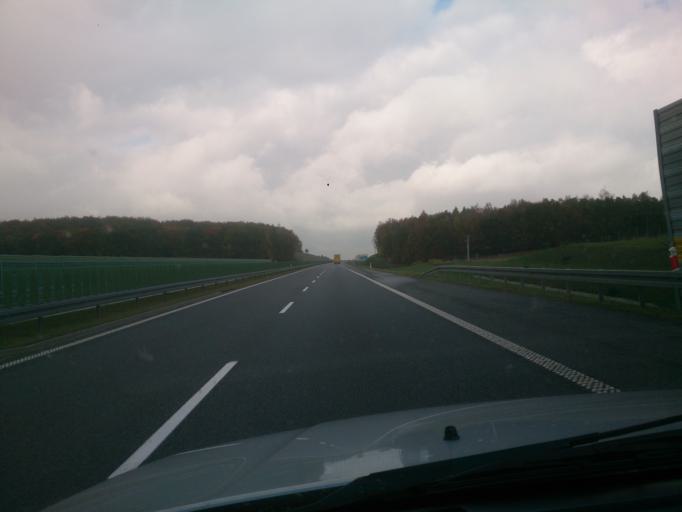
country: PL
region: Pomeranian Voivodeship
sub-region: Powiat tczewski
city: Pelplin
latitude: 53.9179
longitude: 18.6441
